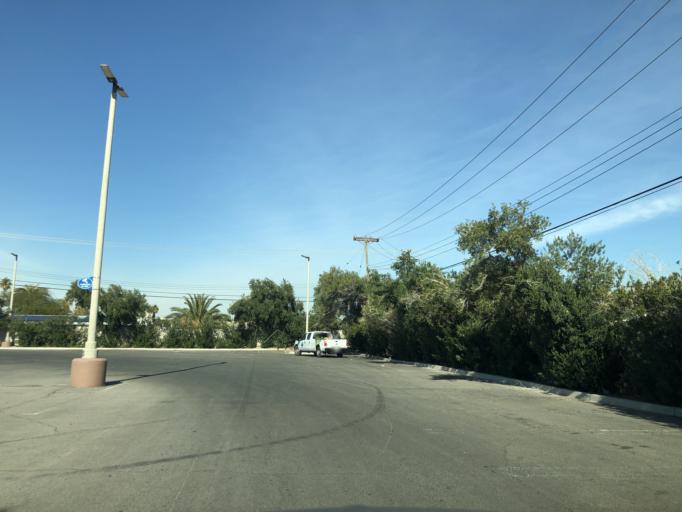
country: US
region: Nevada
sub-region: Clark County
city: Winchester
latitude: 36.1253
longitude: -115.1329
